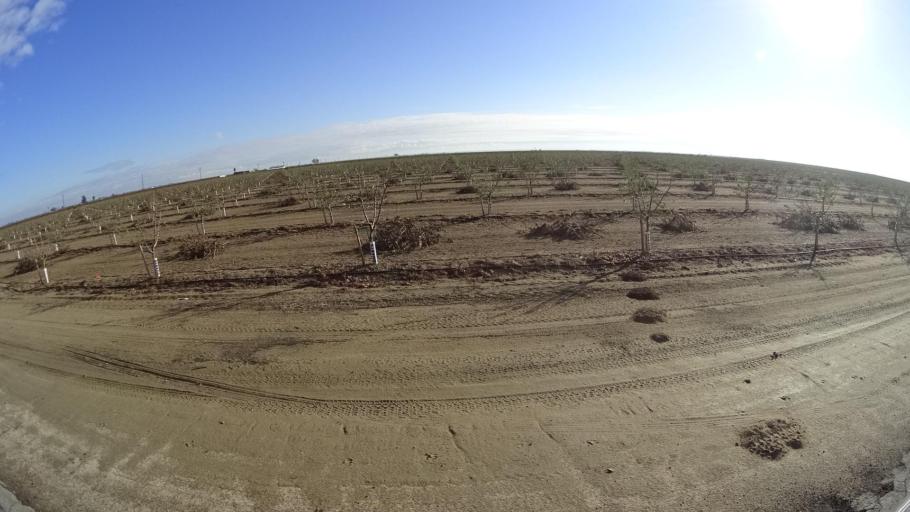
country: US
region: California
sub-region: Kern County
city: Delano
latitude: 35.7157
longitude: -119.3030
